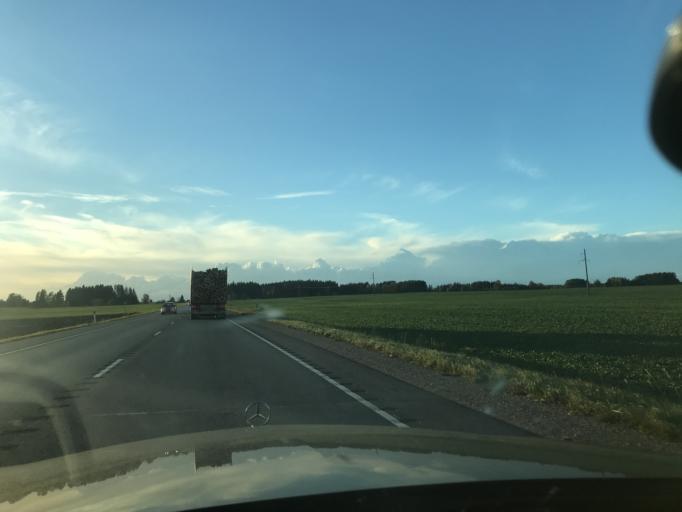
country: EE
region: Vorumaa
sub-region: Voru linn
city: Voru
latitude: 57.8674
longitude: 26.9475
